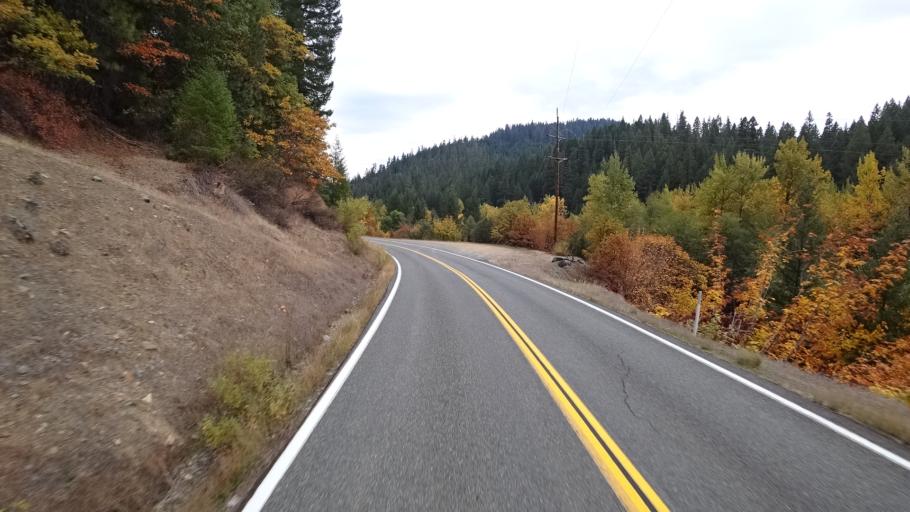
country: US
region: California
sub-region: Siskiyou County
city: Happy Camp
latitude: 41.9120
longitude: -123.4537
